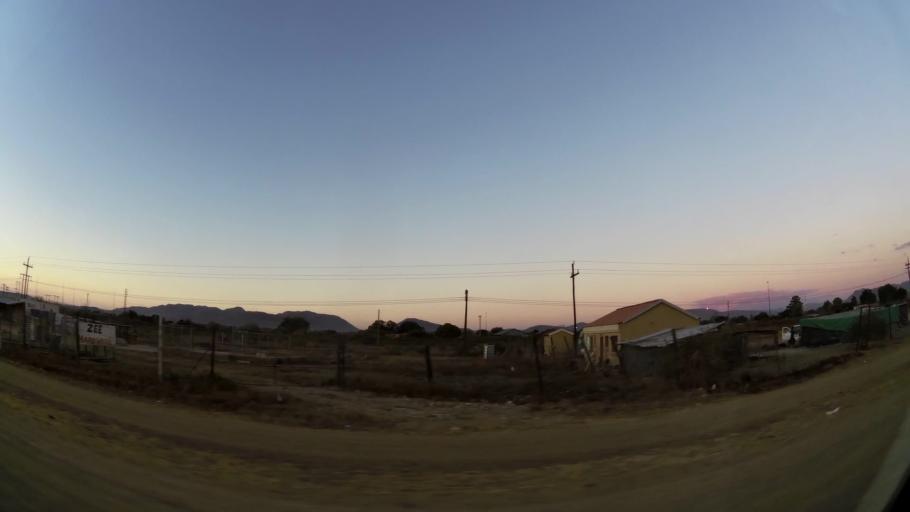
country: ZA
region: Limpopo
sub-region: Waterberg District Municipality
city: Mokopane
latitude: -24.1452
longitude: 28.9703
